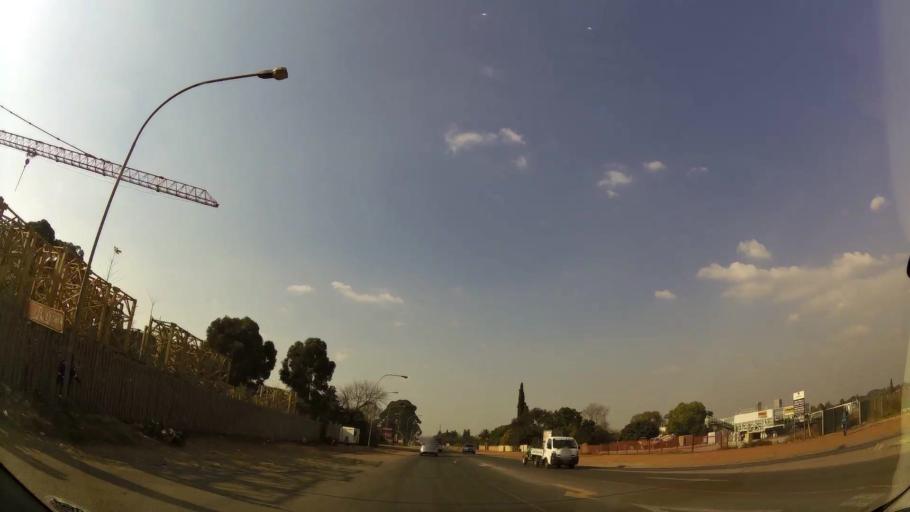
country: ZA
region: Gauteng
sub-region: Ekurhuleni Metropolitan Municipality
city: Tembisa
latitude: -26.0910
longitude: 28.2712
